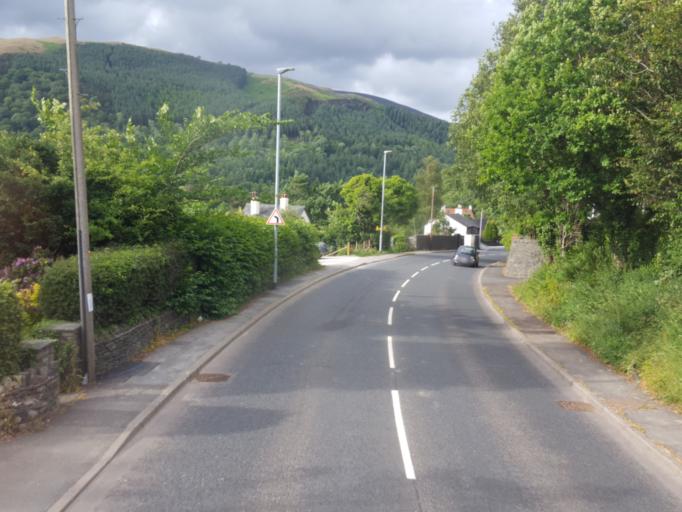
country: GB
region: England
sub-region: Cumbria
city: Keswick
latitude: 54.6005
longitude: -3.1180
